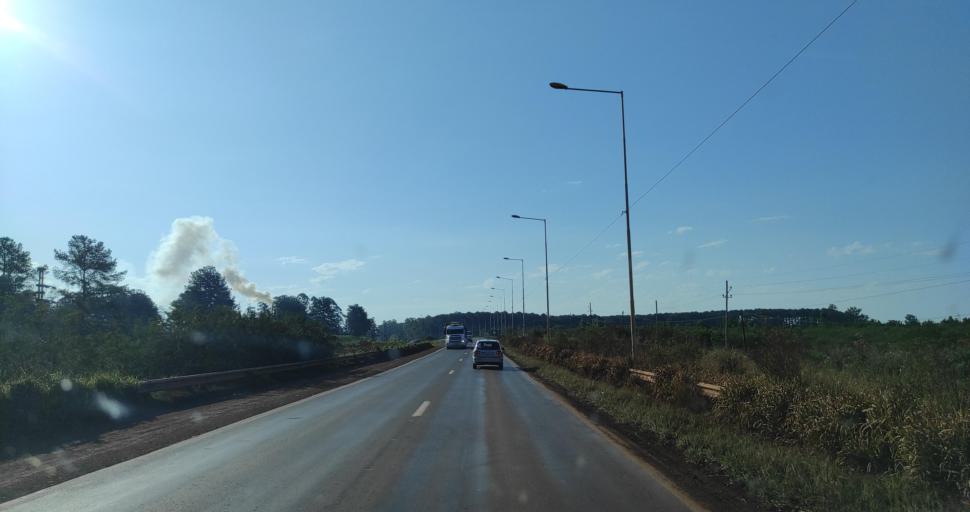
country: AR
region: Corrientes
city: Gobernador Ingeniero Valentin Virasoro
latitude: -28.0233
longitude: -56.0159
